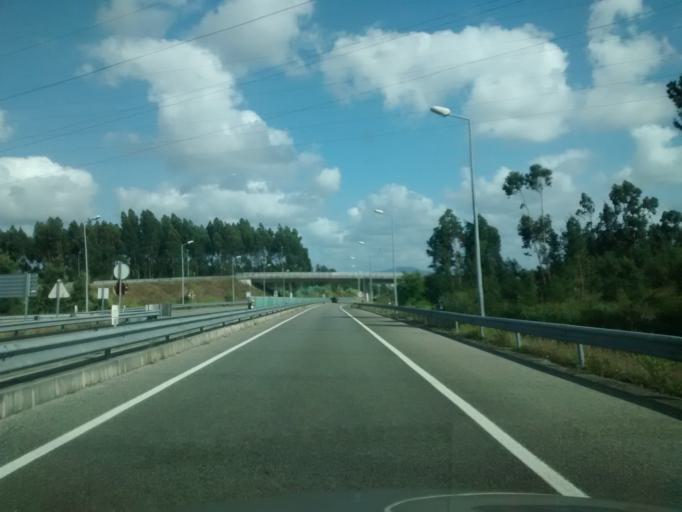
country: PT
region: Aveiro
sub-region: Anadia
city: Sangalhos
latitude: 40.4675
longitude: -8.4655
